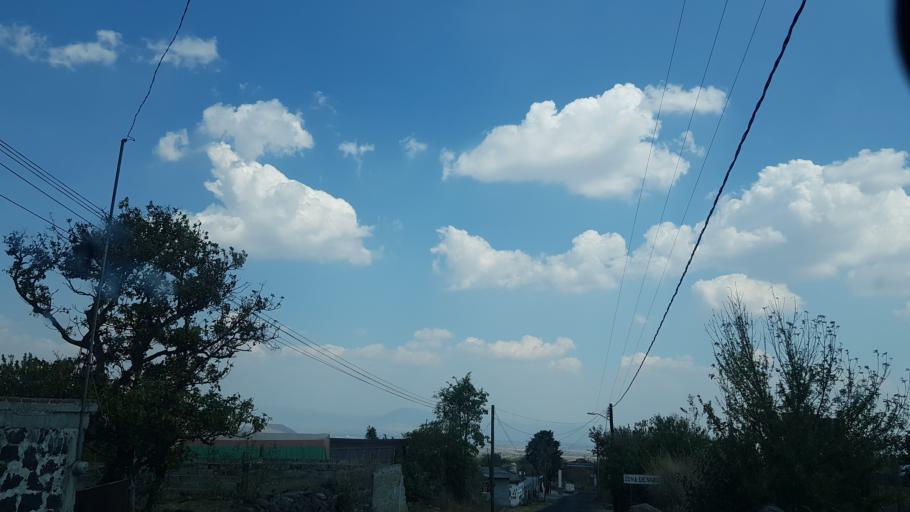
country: MX
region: Puebla
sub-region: Atlixco
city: San Pedro Benito Juarez
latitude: 18.9502
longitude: -98.5419
